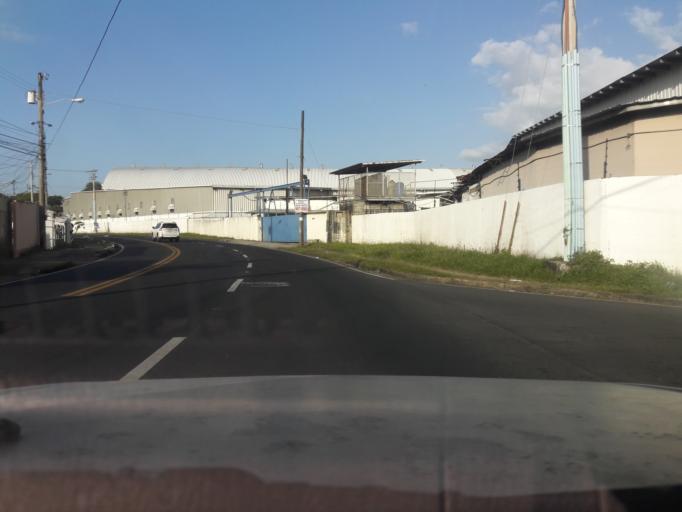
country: PA
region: Panama
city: Panama
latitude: 9.0229
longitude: -79.4974
